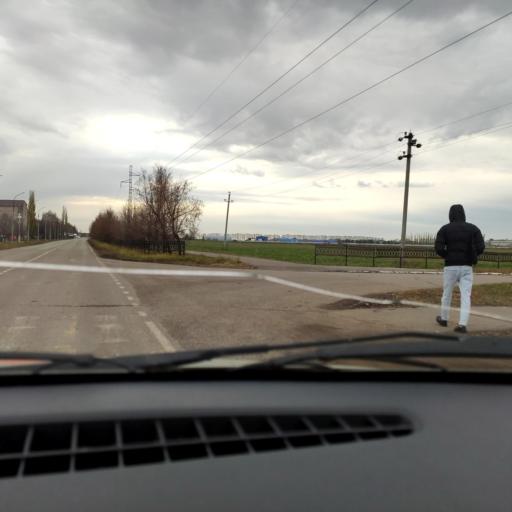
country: RU
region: Bashkortostan
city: Ufa
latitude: 54.8340
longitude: 55.9958
